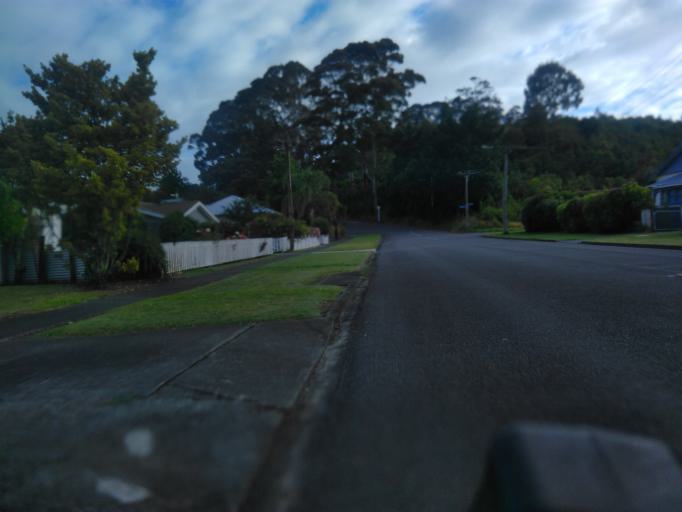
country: NZ
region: Gisborne
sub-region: Gisborne District
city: Gisborne
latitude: -38.6446
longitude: 178.0133
